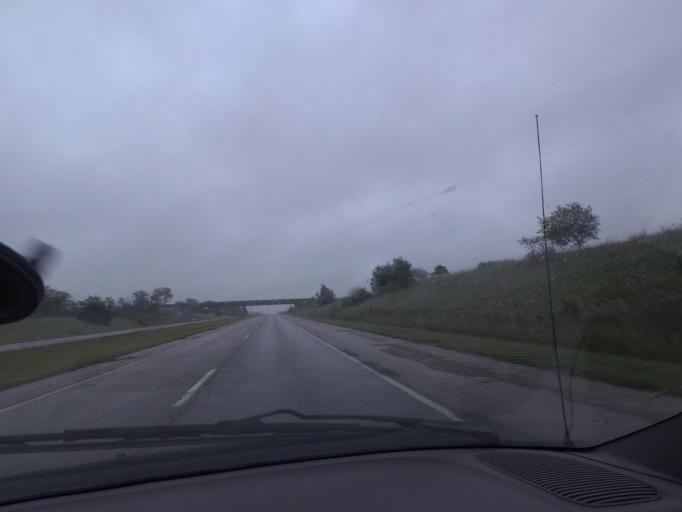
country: US
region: Illinois
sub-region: Pike County
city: Barry
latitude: 39.6897
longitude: -90.9178
